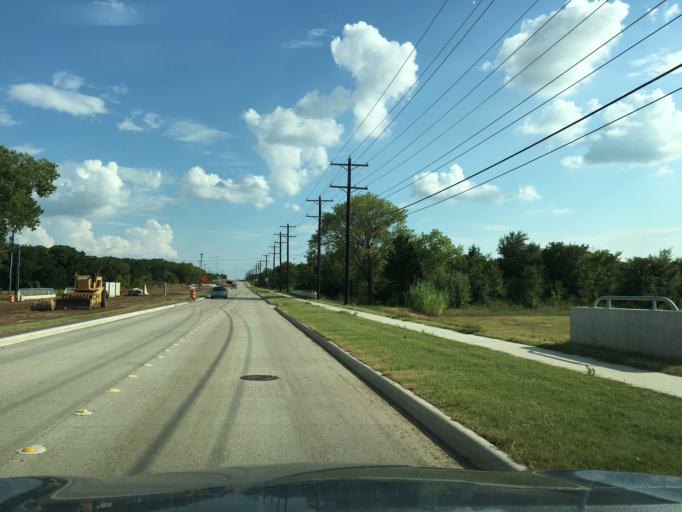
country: US
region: Texas
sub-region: Denton County
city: Denton
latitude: 33.2248
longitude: -97.0833
